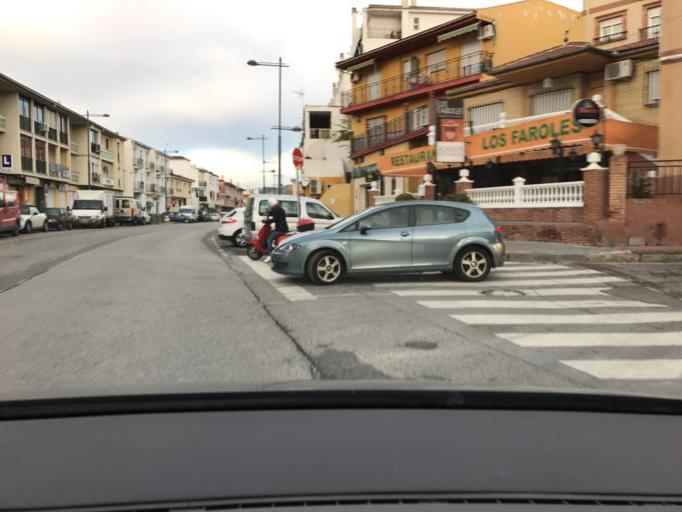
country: ES
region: Andalusia
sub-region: Provincia de Granada
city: Cenes de la Vega
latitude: 37.1603
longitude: -3.5423
